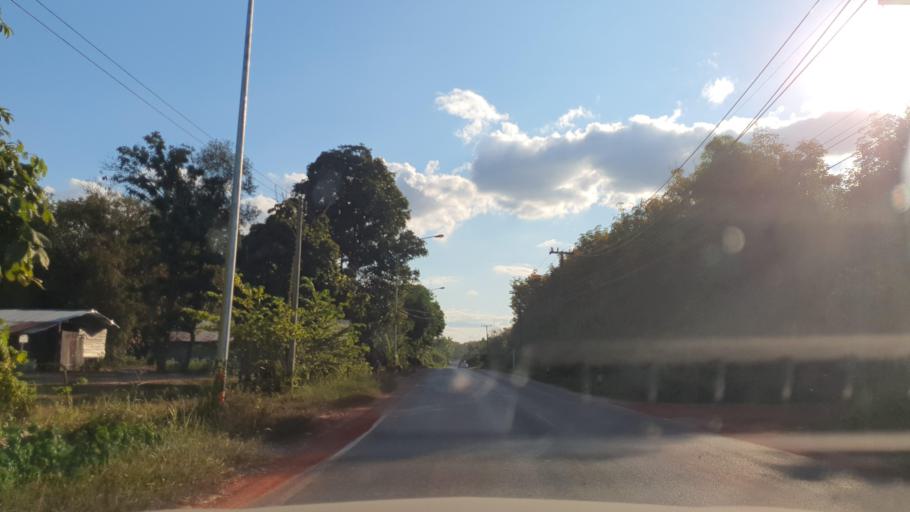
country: TH
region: Changwat Bueng Kan
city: Si Wilai
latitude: 18.1480
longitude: 103.8979
